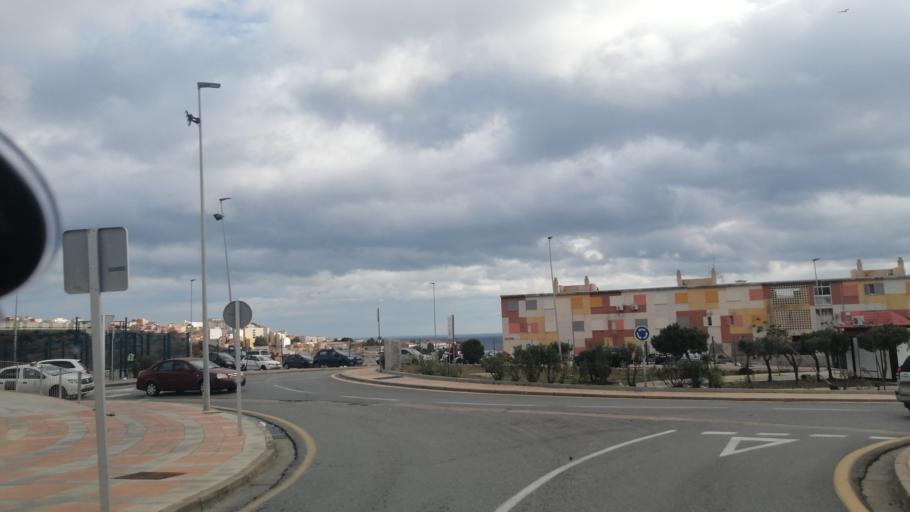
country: ES
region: Ceuta
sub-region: Ceuta
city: Ceuta
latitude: 35.8809
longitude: -5.3402
